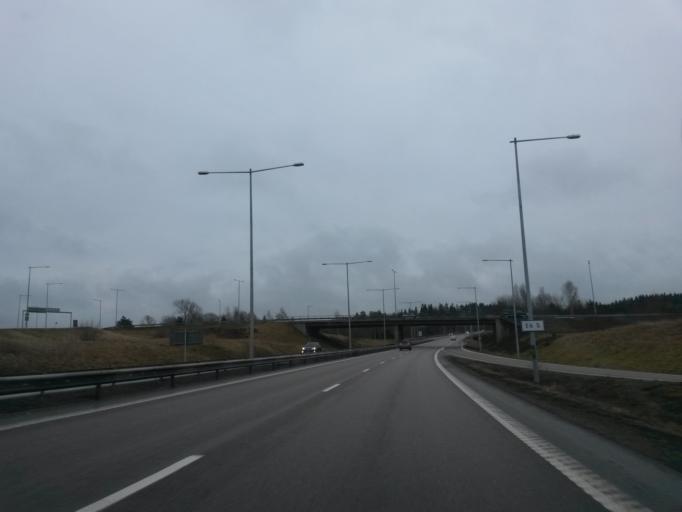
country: SE
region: Vaestra Goetaland
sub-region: Uddevalla Kommun
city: Uddevalla
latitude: 58.3497
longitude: 11.9821
